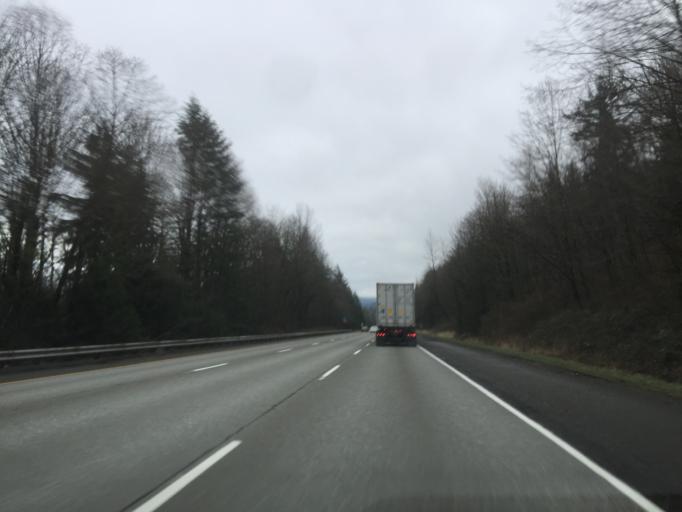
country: US
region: Washington
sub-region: King County
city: Snoqualmie
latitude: 47.5035
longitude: -121.8234
